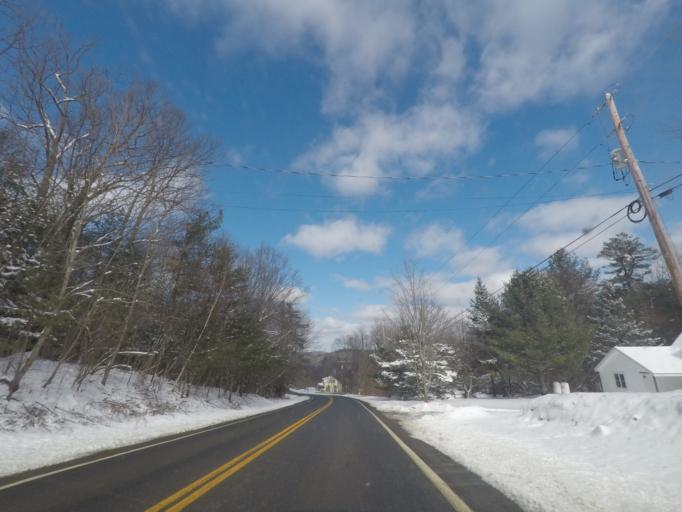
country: US
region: New York
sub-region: Rensselaer County
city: Nassau
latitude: 42.4833
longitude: -73.5200
